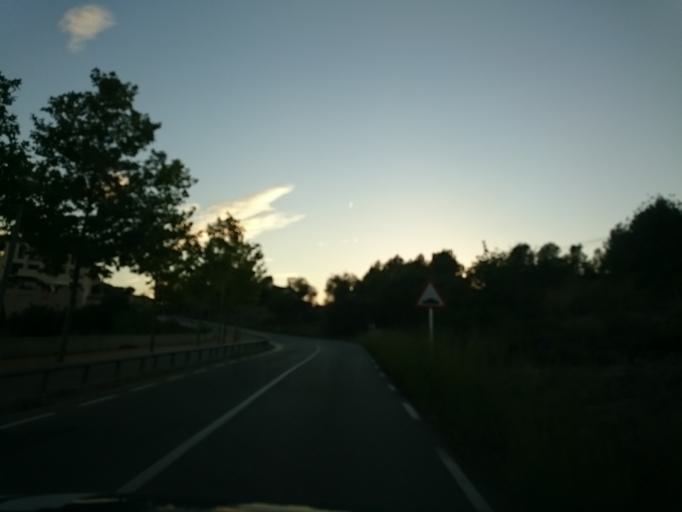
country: ES
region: Catalonia
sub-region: Provincia de Barcelona
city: Sant Pere de Ribes
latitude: 41.2665
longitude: 1.7837
